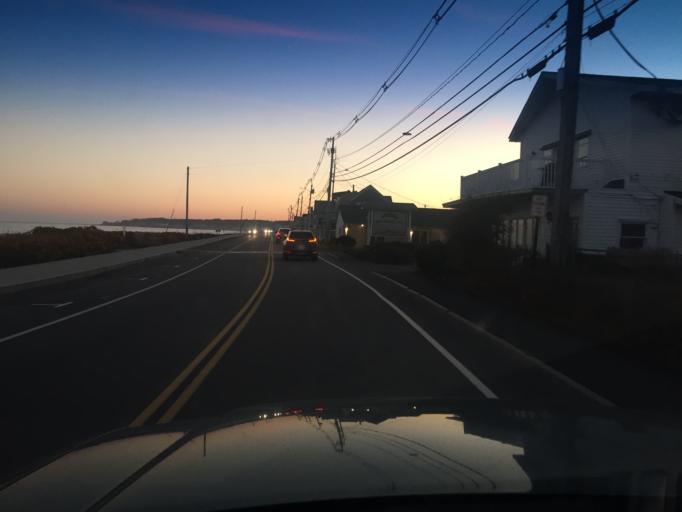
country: US
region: Maine
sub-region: York County
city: York Beach
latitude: 43.1577
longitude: -70.6224
